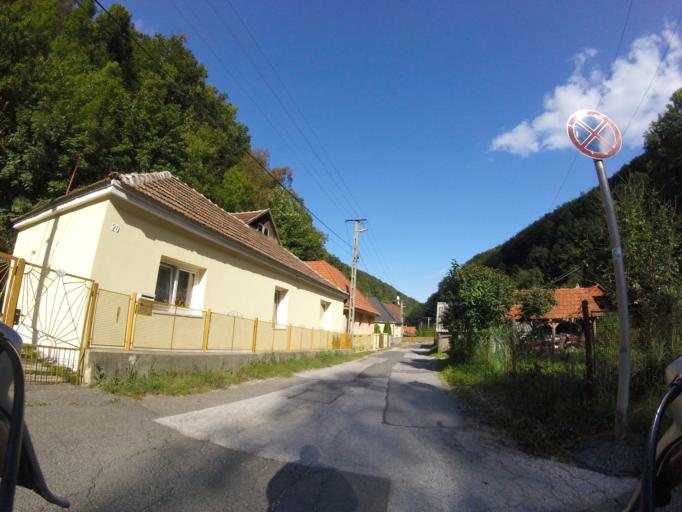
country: HU
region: Heves
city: Szilvasvarad
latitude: 48.1104
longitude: 20.5327
